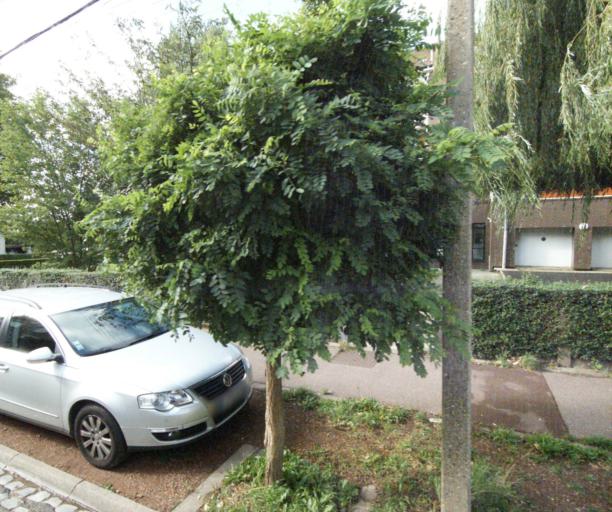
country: FR
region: Nord-Pas-de-Calais
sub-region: Departement du Nord
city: Lomme
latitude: 50.6435
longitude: 2.9940
